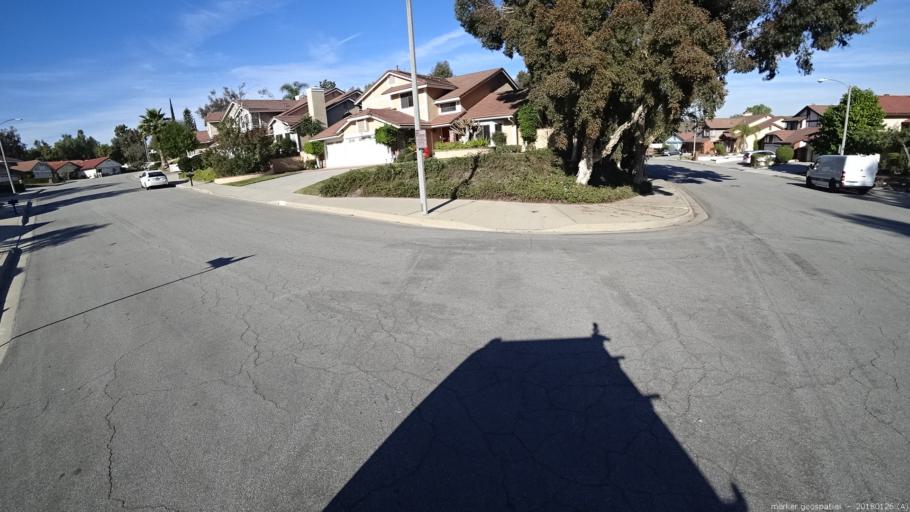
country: US
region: California
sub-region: San Bernardino County
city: Chino Hills
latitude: 33.9939
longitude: -117.7926
